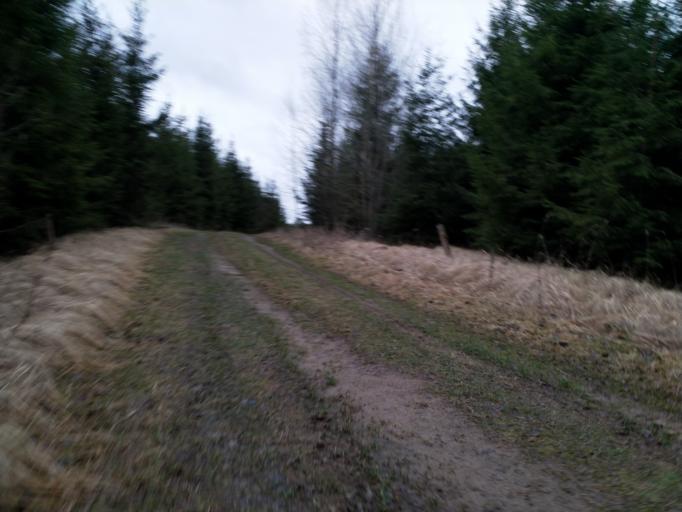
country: LV
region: Saldus Rajons
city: Saldus
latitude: 56.8938
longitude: 22.3299
